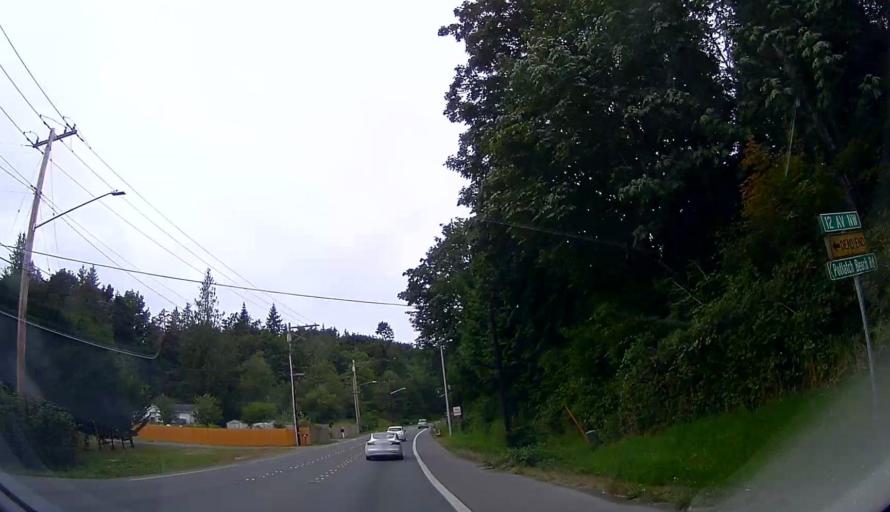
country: US
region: Washington
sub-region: Snohomish County
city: Tulalip
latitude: 48.0399
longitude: -122.2492
